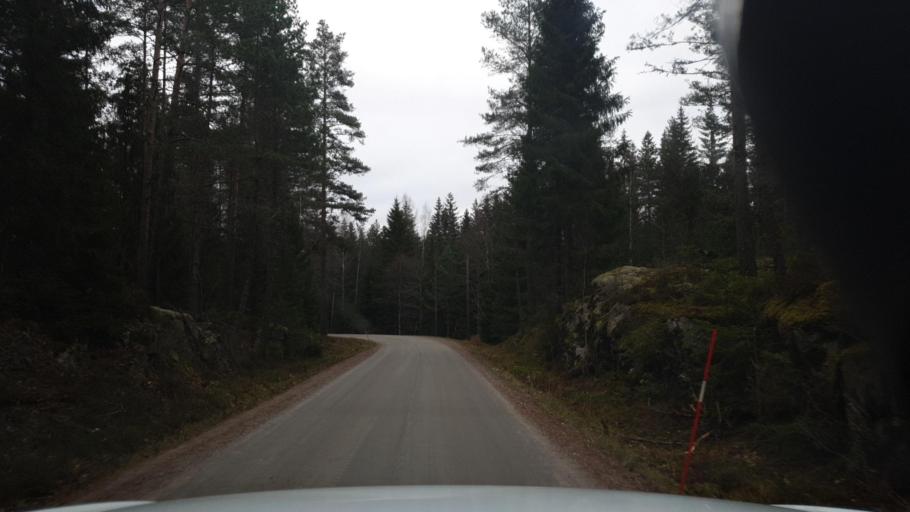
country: SE
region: Vaermland
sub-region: Karlstads Kommun
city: Edsvalla
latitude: 59.5359
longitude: 12.9960
